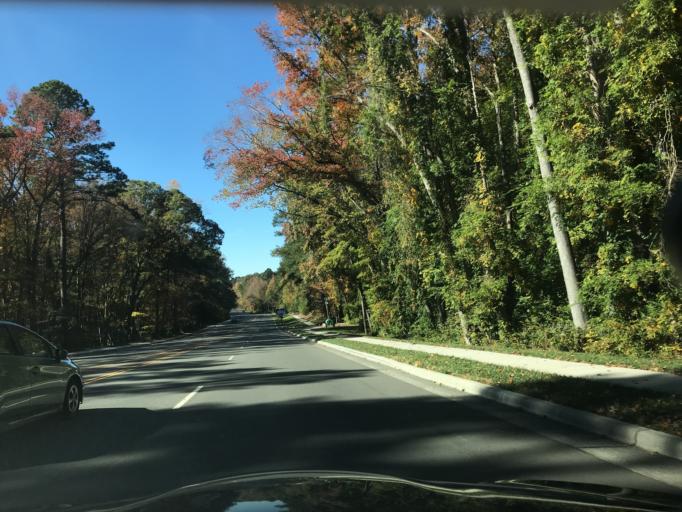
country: US
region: North Carolina
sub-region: Durham County
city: Durham
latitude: 35.9966
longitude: -78.9494
